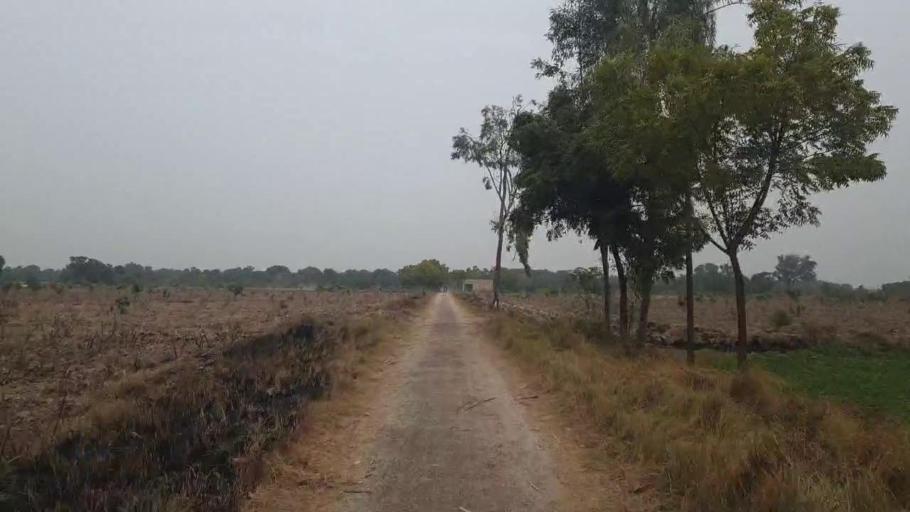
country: PK
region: Sindh
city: Tando Adam
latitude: 25.8156
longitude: 68.6695
